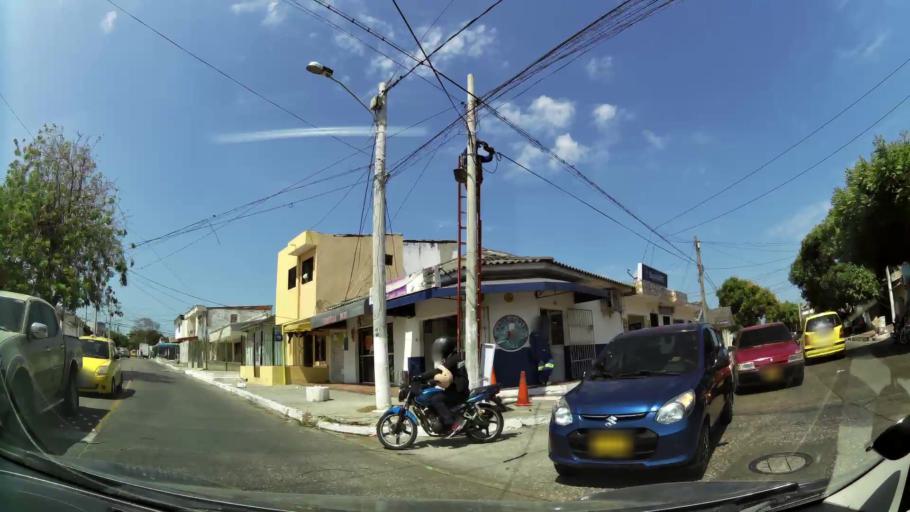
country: CO
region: Atlantico
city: Barranquilla
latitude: 10.9634
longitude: -74.8027
